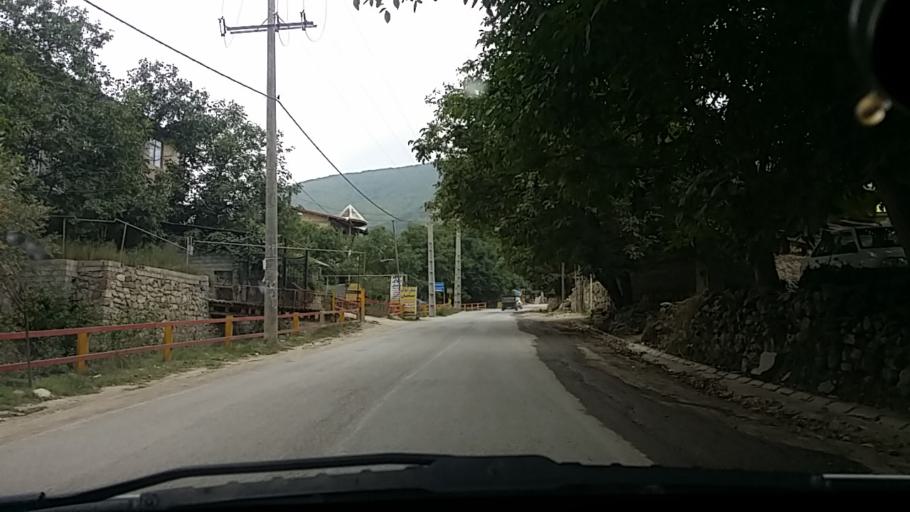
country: IR
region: Mazandaran
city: `Abbasabad
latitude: 36.4851
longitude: 51.1336
